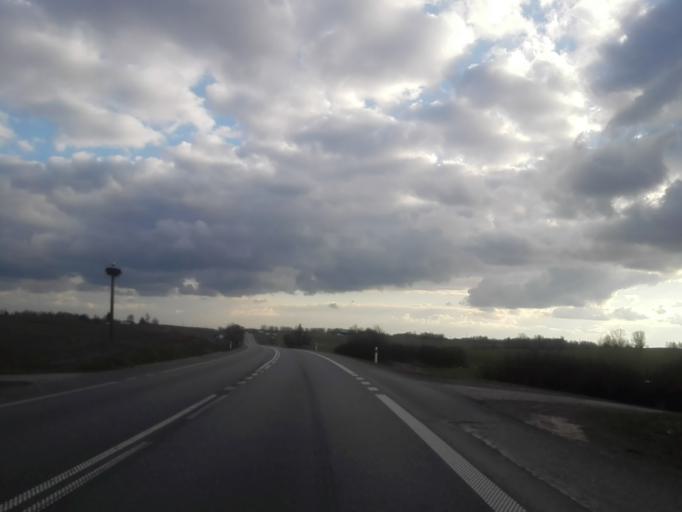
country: PL
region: Podlasie
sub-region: Suwalki
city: Suwalki
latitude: 54.2087
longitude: 23.0263
